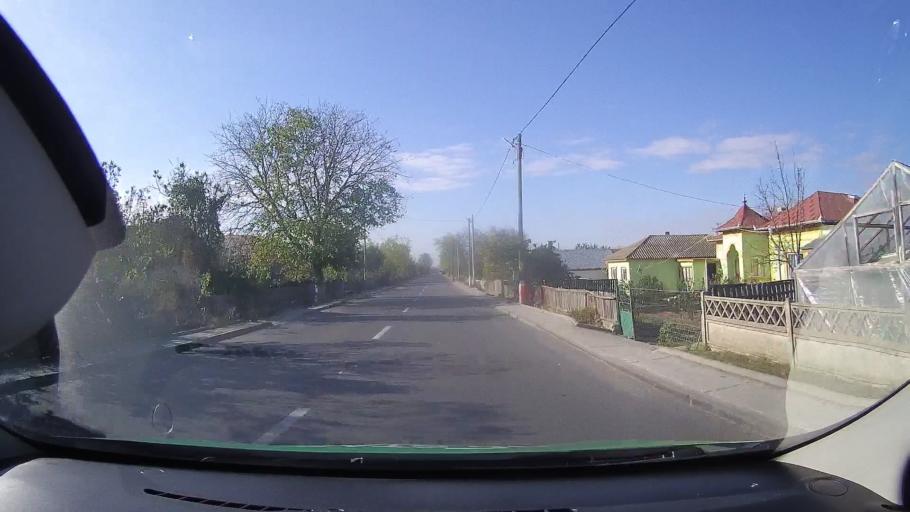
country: RO
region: Tulcea
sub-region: Comuna Murighiol
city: Murighiol
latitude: 45.0239
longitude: 29.1317
